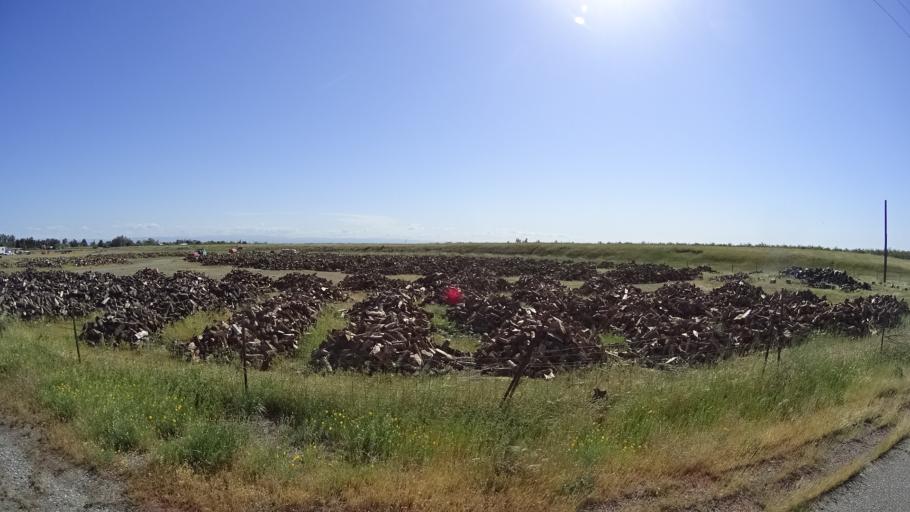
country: US
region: California
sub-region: Glenn County
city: Orland
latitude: 39.7224
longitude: -122.1692
